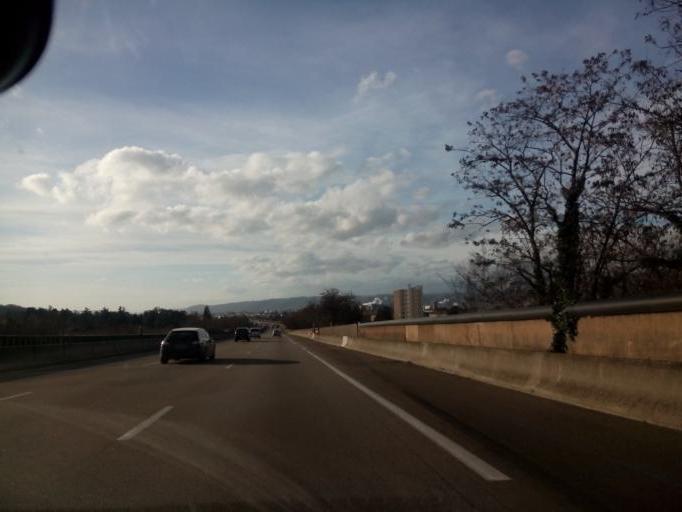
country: FR
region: Rhone-Alpes
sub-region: Departement de l'Isere
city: Roussillon
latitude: 45.3682
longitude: 4.8057
